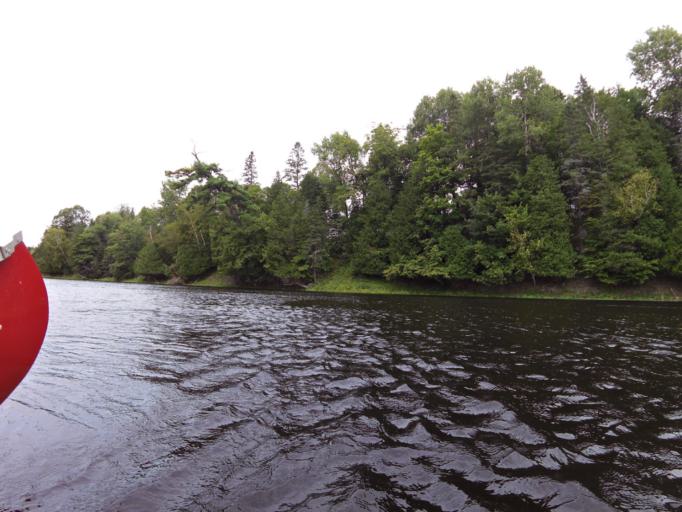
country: CA
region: Quebec
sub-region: Outaouais
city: Wakefield
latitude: 45.7633
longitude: -75.9227
